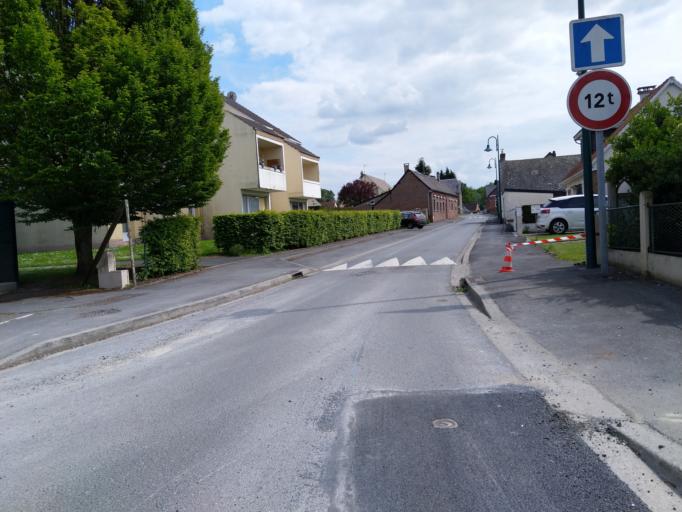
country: FR
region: Picardie
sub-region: Departement de l'Aisne
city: Boue
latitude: 50.0105
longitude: 3.6958
